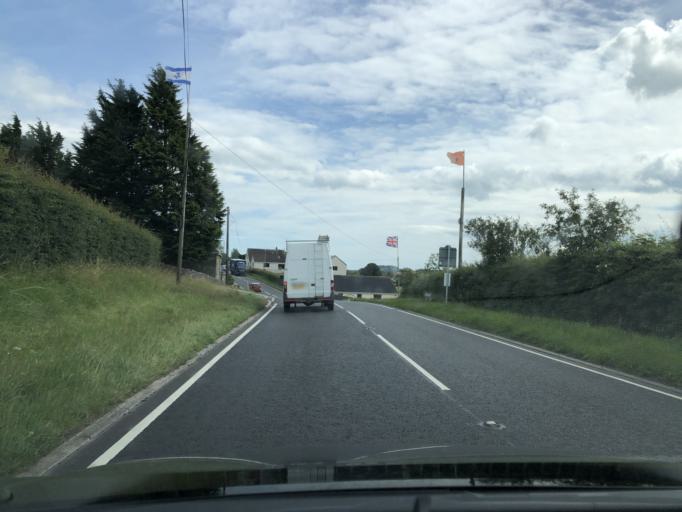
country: GB
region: Northern Ireland
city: Ballynahinch
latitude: 54.4307
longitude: -5.9299
